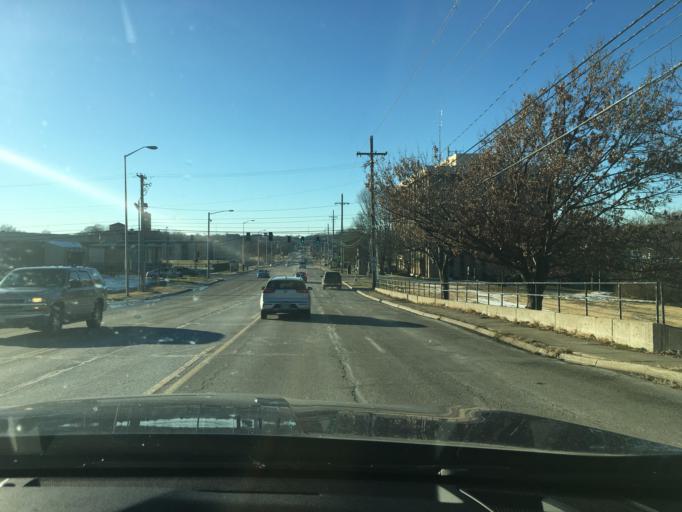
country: US
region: Kansas
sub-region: Johnson County
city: Mission Hills
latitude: 39.0129
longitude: -94.5635
